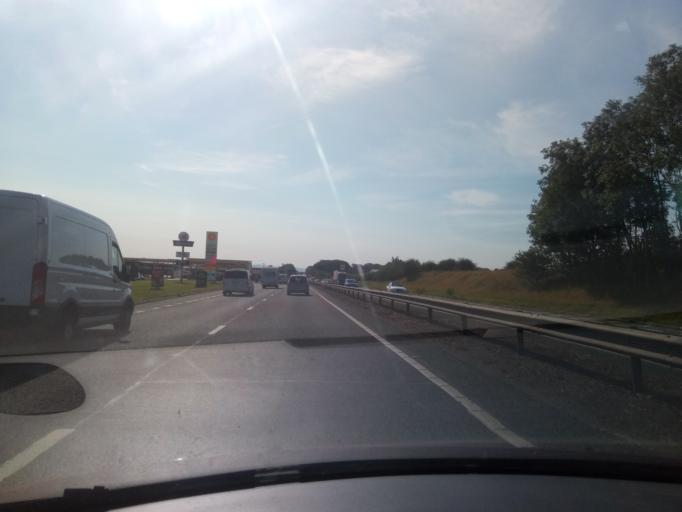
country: GB
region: England
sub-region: Hartlepool
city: Elwick
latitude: 54.6569
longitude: -1.3040
